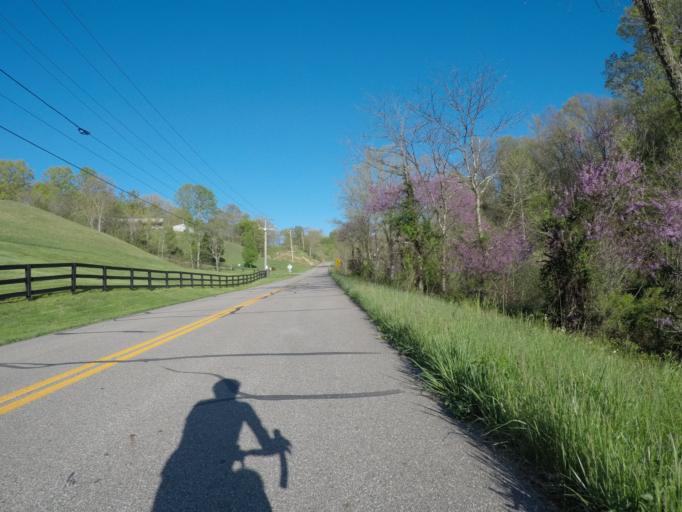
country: US
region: Kentucky
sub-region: Boyd County
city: Meads
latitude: 38.3709
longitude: -82.6580
